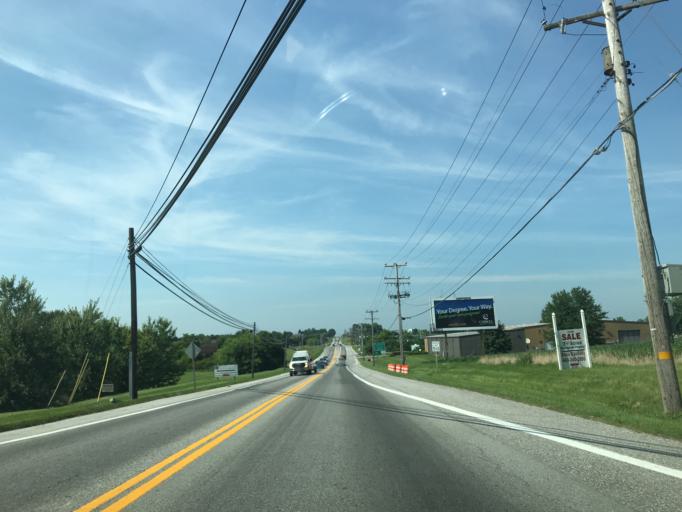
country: US
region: Maryland
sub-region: Carroll County
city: Westminster
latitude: 39.6027
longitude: -76.9986
